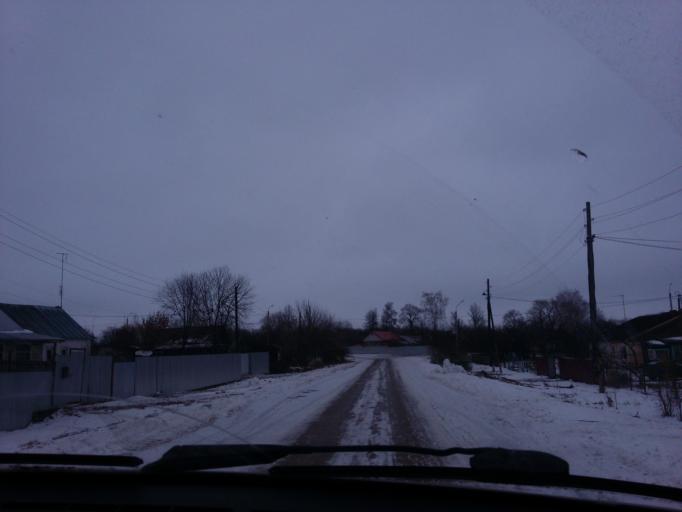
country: RU
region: Tula
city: Plavsk
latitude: 53.8138
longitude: 37.3896
